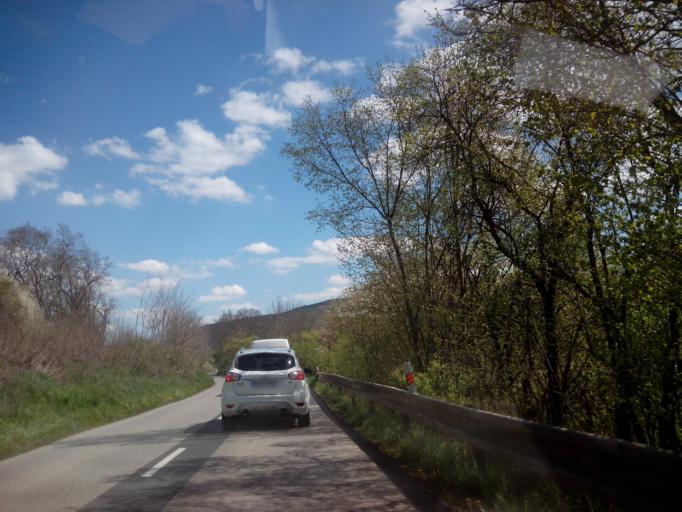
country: CZ
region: Central Bohemia
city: Hyskov
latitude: 49.9926
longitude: 14.0304
